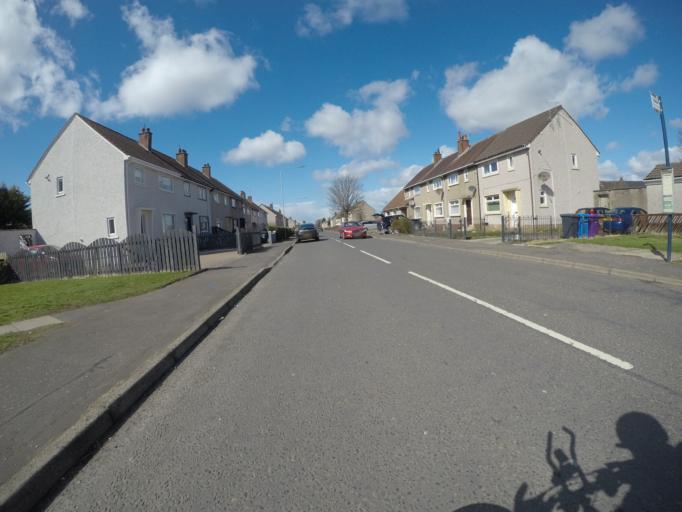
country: GB
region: Scotland
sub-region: North Ayrshire
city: Irvine
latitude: 55.6223
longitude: -4.6537
